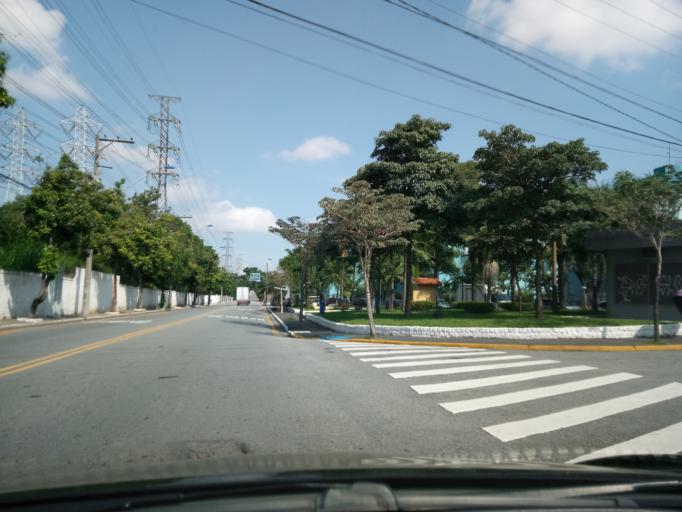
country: BR
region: Sao Paulo
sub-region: Sao Caetano Do Sul
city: Sao Caetano do Sul
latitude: -23.6358
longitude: -46.5755
